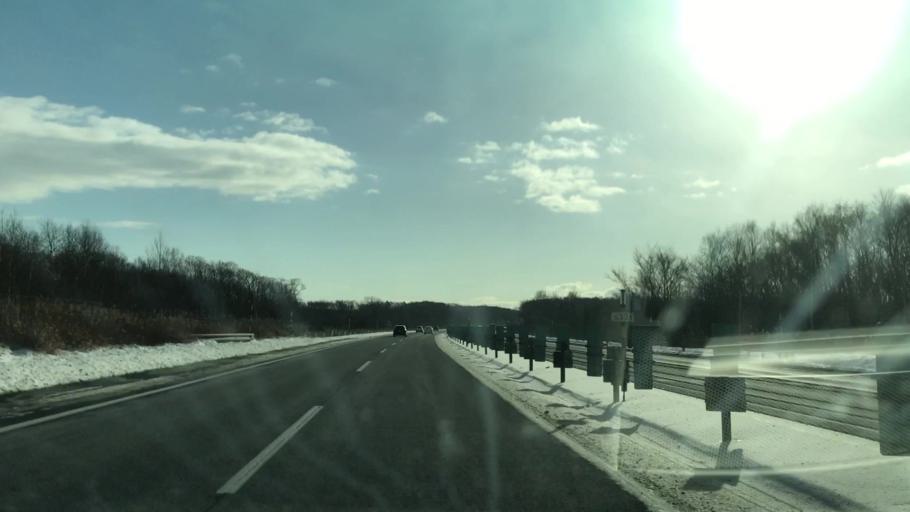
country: JP
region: Hokkaido
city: Chitose
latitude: 42.8377
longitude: 141.6042
